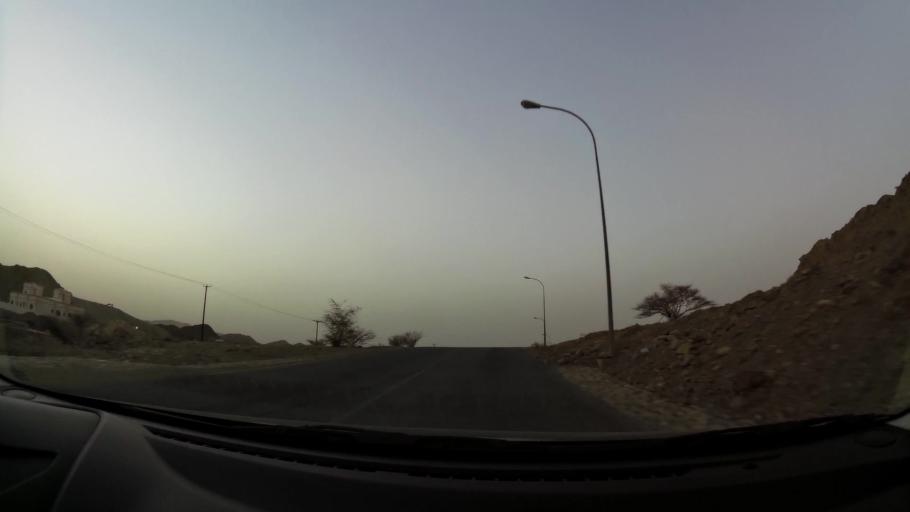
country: OM
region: Muhafazat Masqat
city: Bawshar
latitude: 23.4982
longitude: 58.3443
